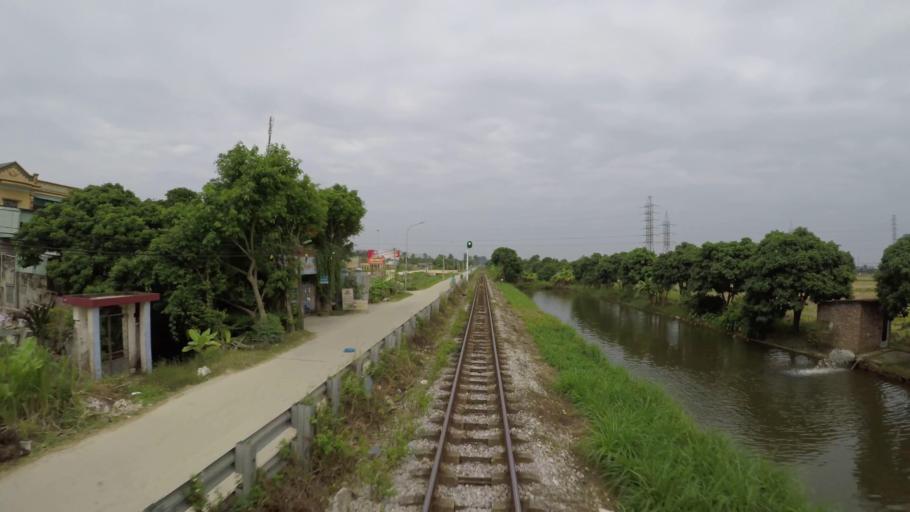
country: VN
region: Hai Duong
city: Lai Cach
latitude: 20.9503
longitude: 106.2431
